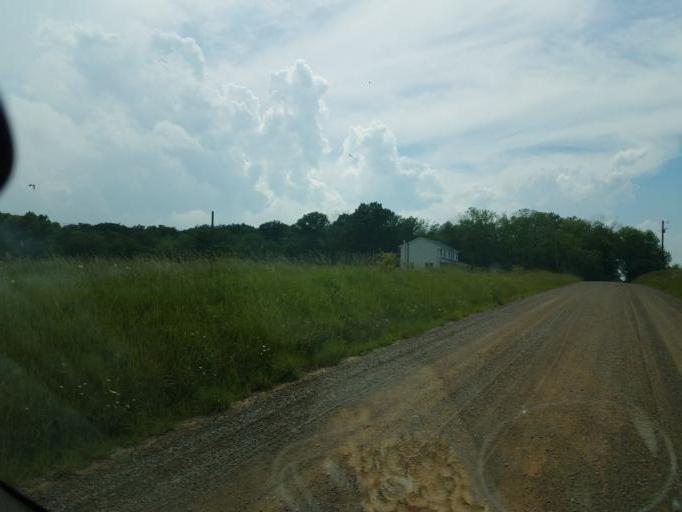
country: US
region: Ohio
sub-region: Knox County
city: Oak Hill
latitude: 40.3053
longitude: -82.2468
